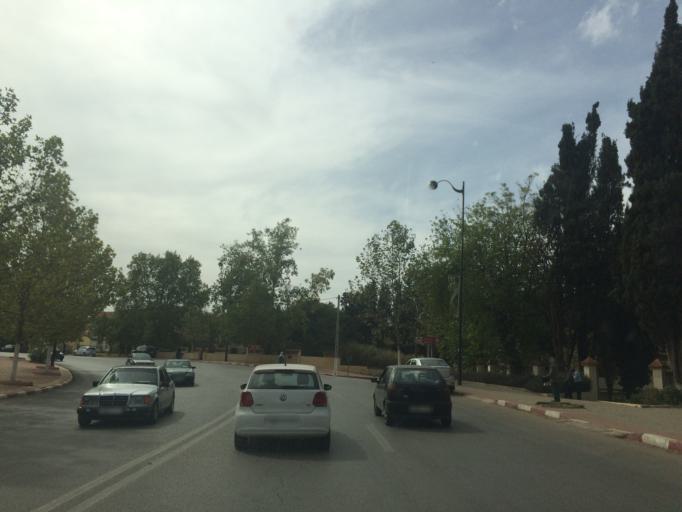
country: MA
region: Meknes-Tafilalet
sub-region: El-Hajeb
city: El Hajeb
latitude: 33.6834
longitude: -5.3729
